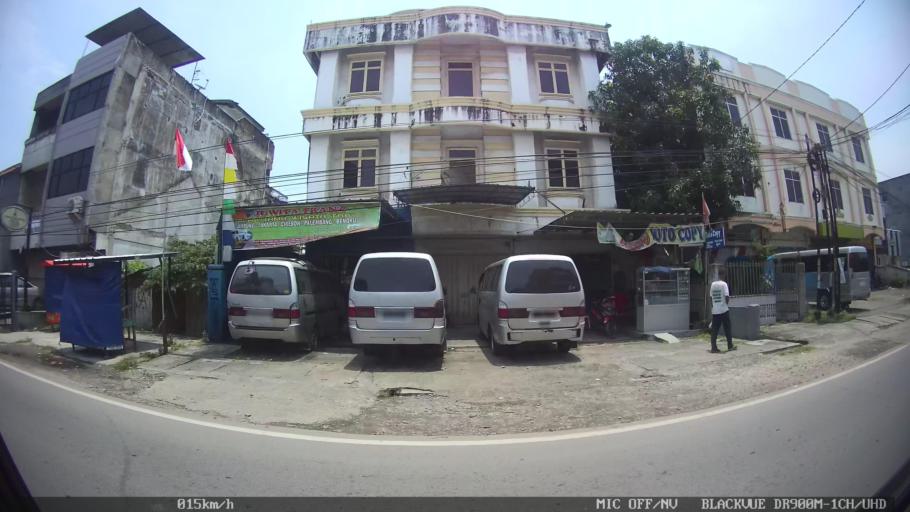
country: ID
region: Lampung
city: Bandarlampung
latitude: -5.4484
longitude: 105.2613
